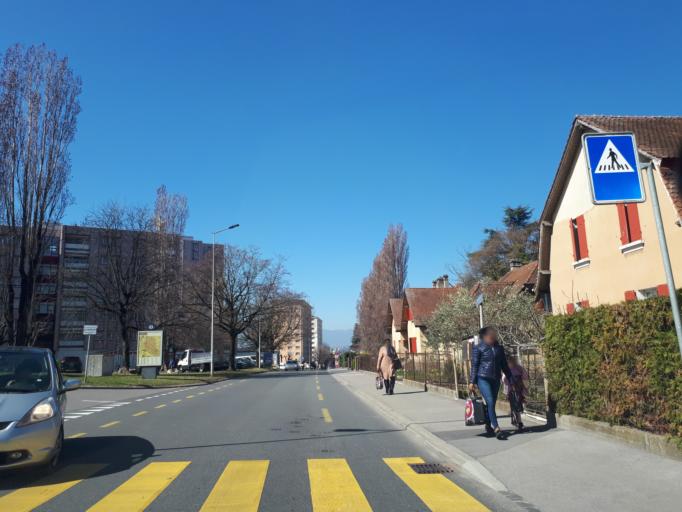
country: CH
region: Vaud
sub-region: Ouest Lausannois District
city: Prilly
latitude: 46.5251
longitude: 6.5980
